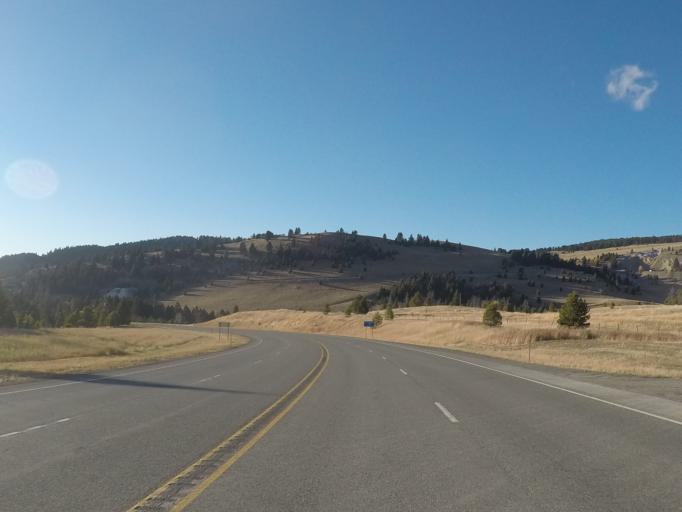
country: US
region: Montana
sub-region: Lewis and Clark County
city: Helena West Side
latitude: 46.5619
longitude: -112.3738
